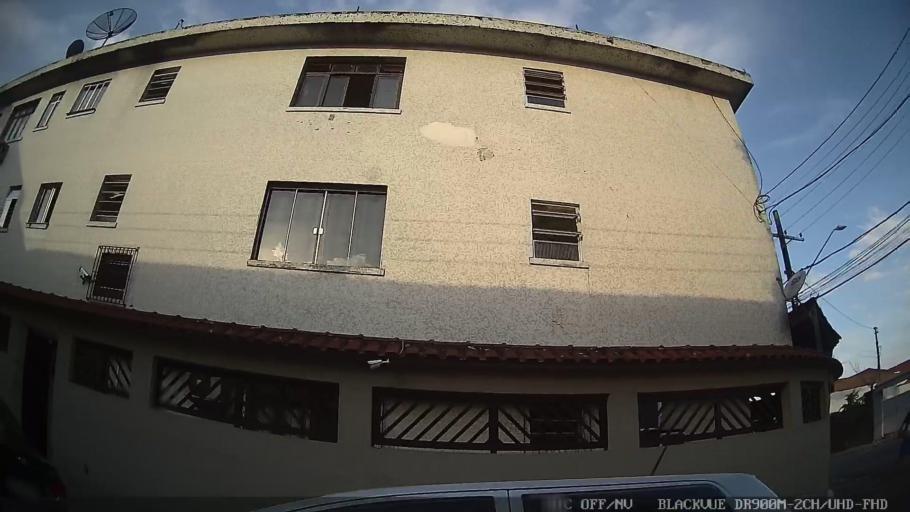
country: BR
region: Sao Paulo
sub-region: Cubatao
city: Cubatao
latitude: -23.8938
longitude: -46.4237
